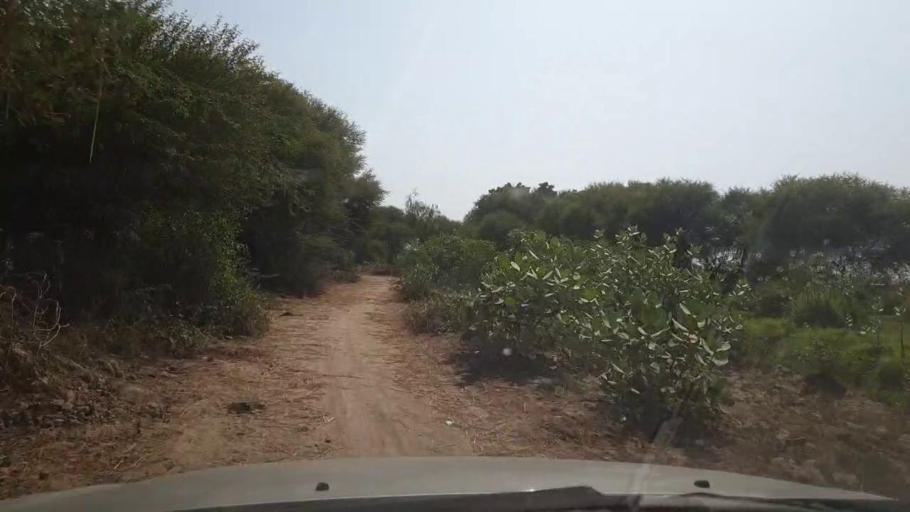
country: PK
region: Sindh
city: Bulri
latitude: 24.8690
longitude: 68.3108
